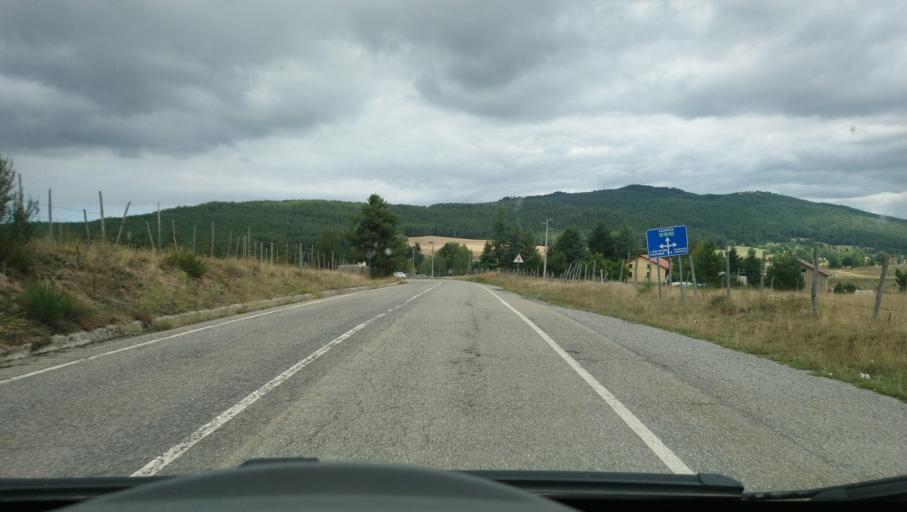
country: IT
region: Calabria
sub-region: Provincia di Cosenza
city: Longobucco
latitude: 39.3129
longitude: 16.5426
